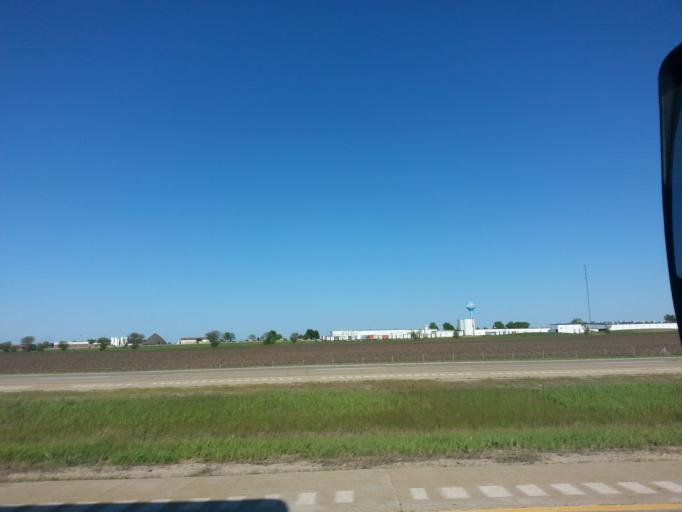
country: US
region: Illinois
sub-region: Marshall County
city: Wenona
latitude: 41.0399
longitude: -89.0566
